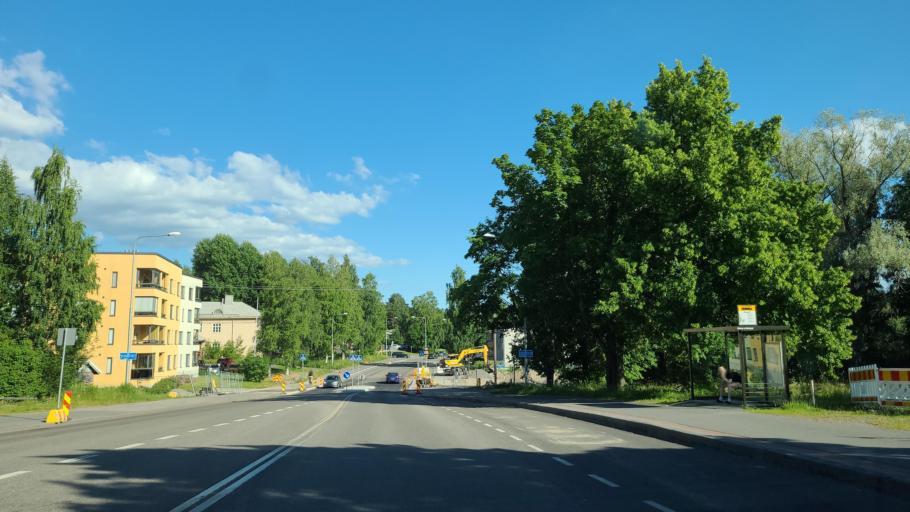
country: FI
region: Central Finland
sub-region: Jyvaeskylae
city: Jyvaeskylae
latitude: 62.2500
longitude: 25.7769
